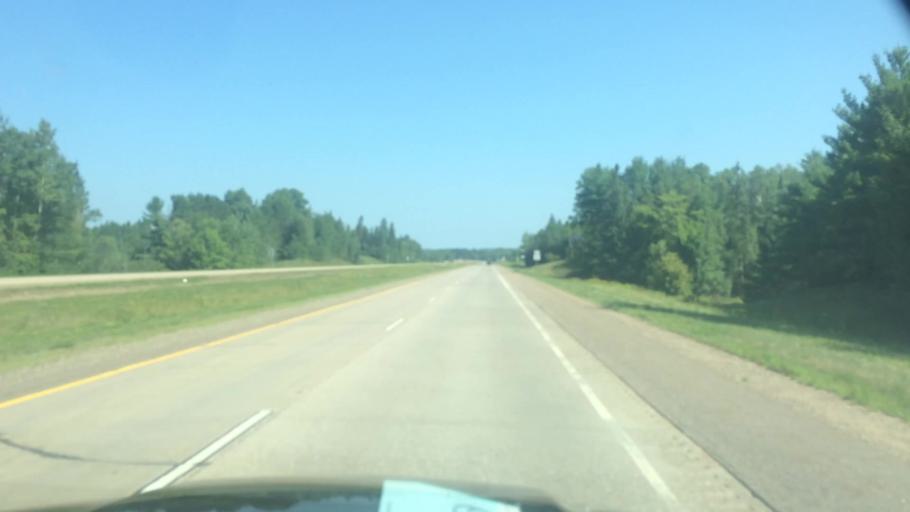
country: US
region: Wisconsin
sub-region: Lincoln County
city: Tomahawk
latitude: 45.3623
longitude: -89.6668
